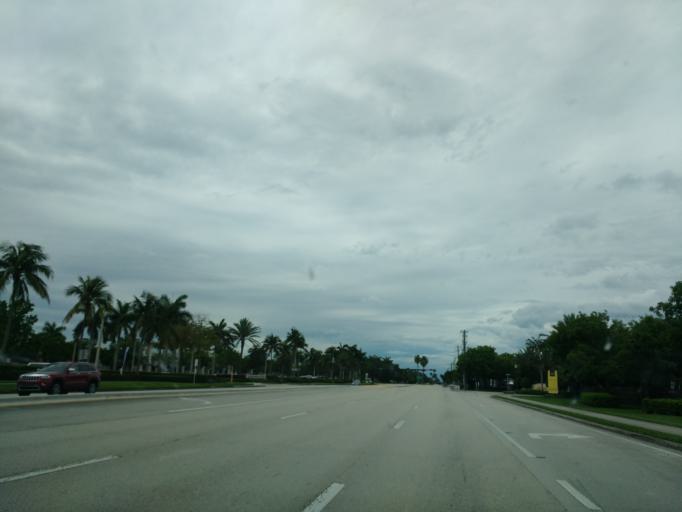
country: US
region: Florida
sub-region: Broward County
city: Pine Island Ridge
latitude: 26.1218
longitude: -80.3300
